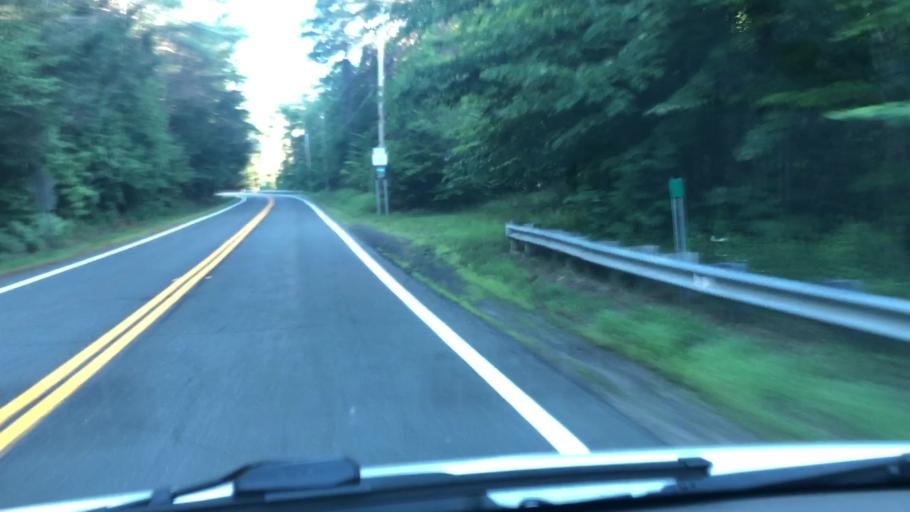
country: US
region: Massachusetts
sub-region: Hampshire County
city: Chesterfield
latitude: 42.3705
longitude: -72.9111
